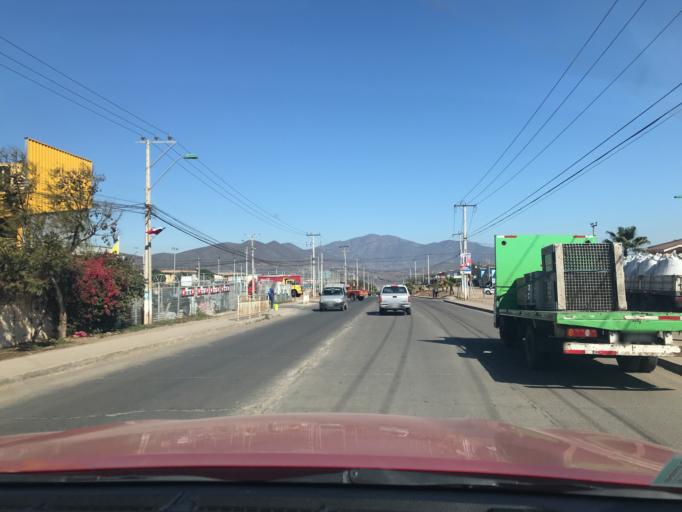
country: CL
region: Coquimbo
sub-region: Provincia de Limari
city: Ovalle
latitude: -30.5845
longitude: -71.1900
